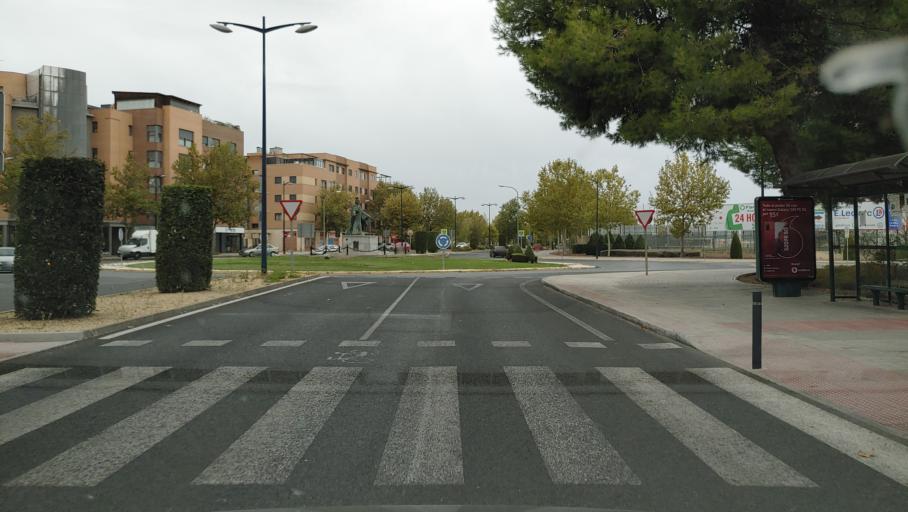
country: ES
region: Castille-La Mancha
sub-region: Provincia de Ciudad Real
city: Ciudad Real
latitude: 38.9727
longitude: -3.9351
